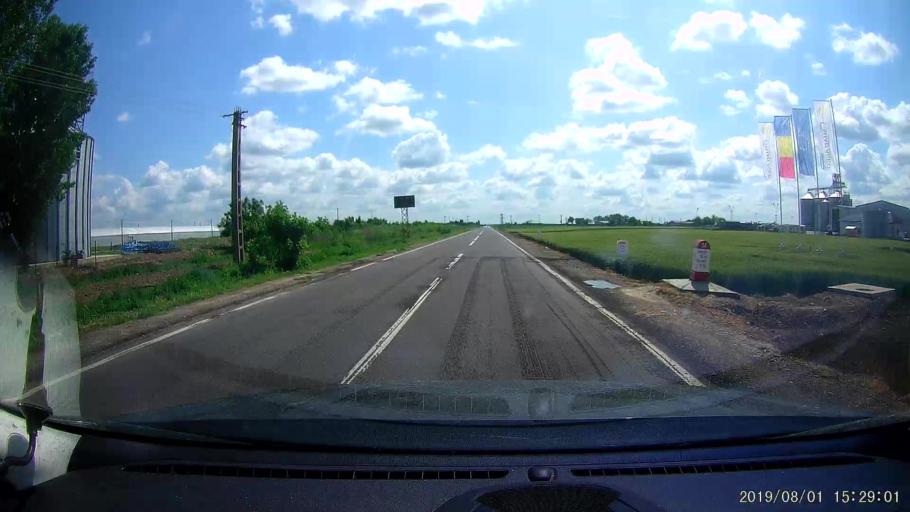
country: RO
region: Braila
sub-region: Comuna Viziru
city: Viziru
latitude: 44.9884
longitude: 27.7036
